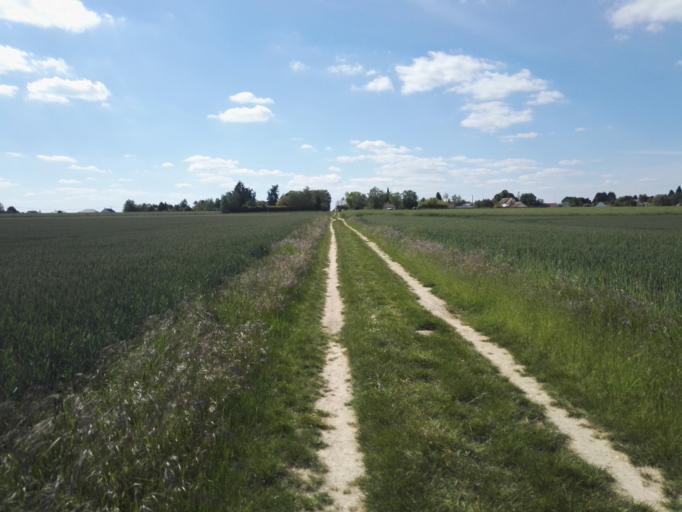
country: FR
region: Haute-Normandie
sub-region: Departement de l'Eure
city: Menilles
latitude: 49.0059
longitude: 1.3142
